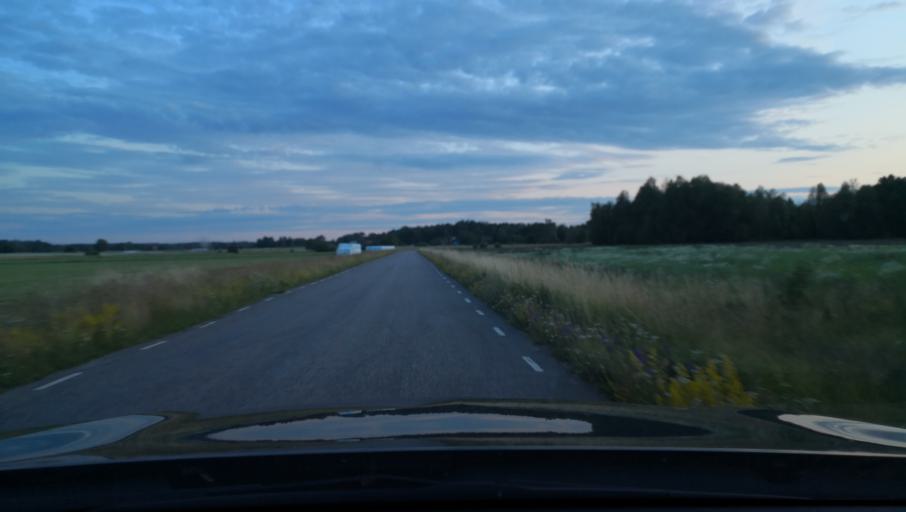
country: SE
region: Uppsala
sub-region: Osthammars Kommun
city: Bjorklinge
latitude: 60.0482
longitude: 17.5071
